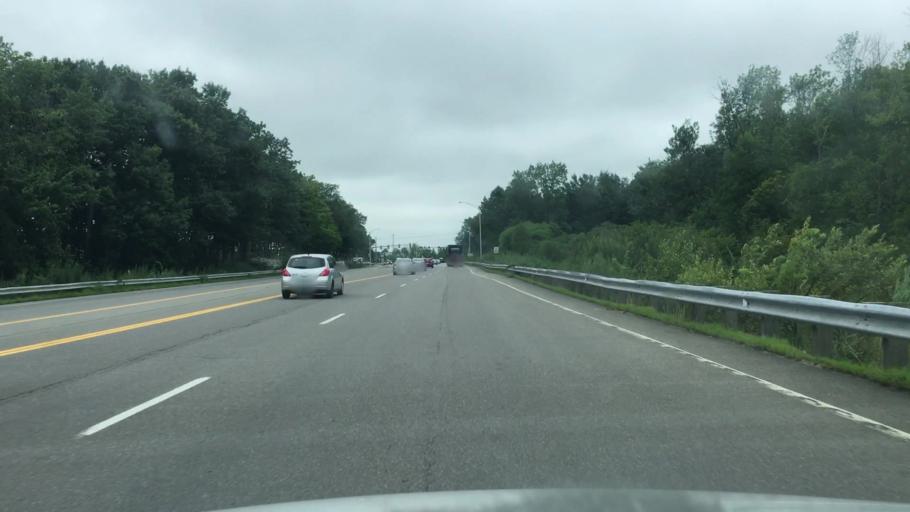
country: US
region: New Hampshire
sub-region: Rockingham County
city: Greenland
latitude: 43.0469
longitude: -70.8175
